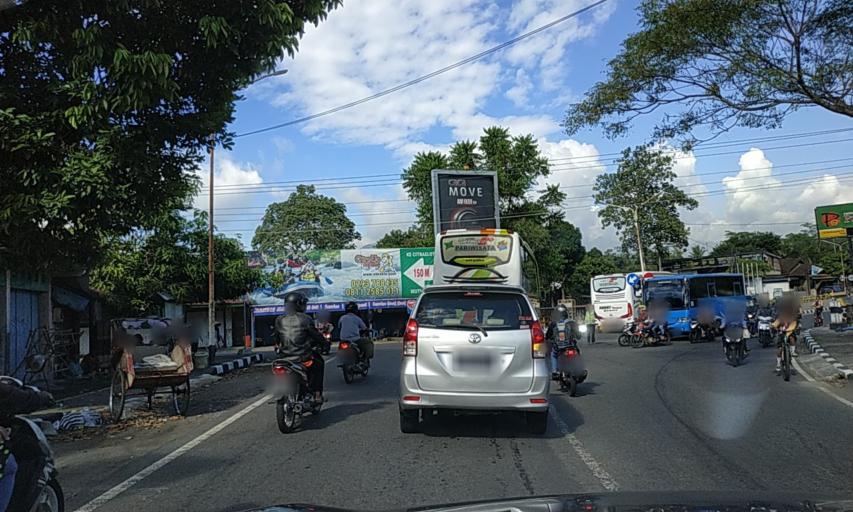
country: ID
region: Central Java
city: Muntilan
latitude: -7.6065
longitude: 110.2290
